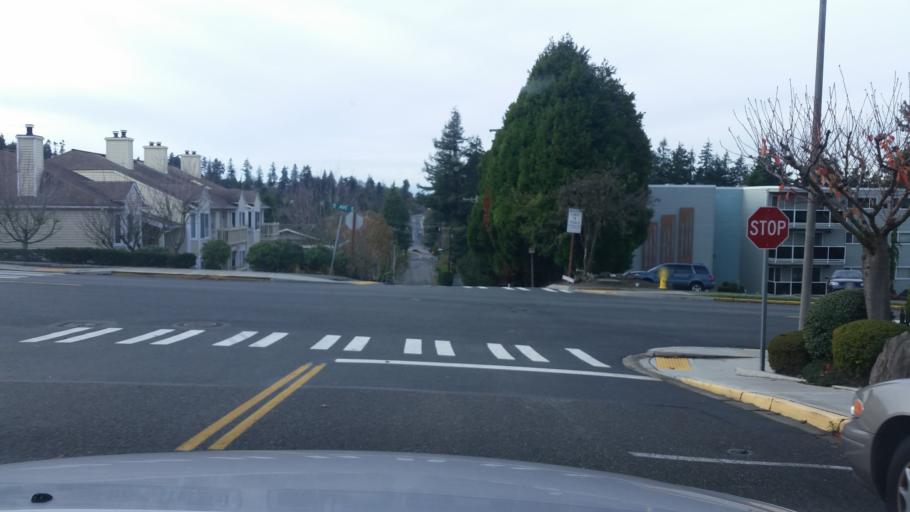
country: US
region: Washington
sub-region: Snohomish County
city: Edmonds
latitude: 47.8032
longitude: -122.3773
